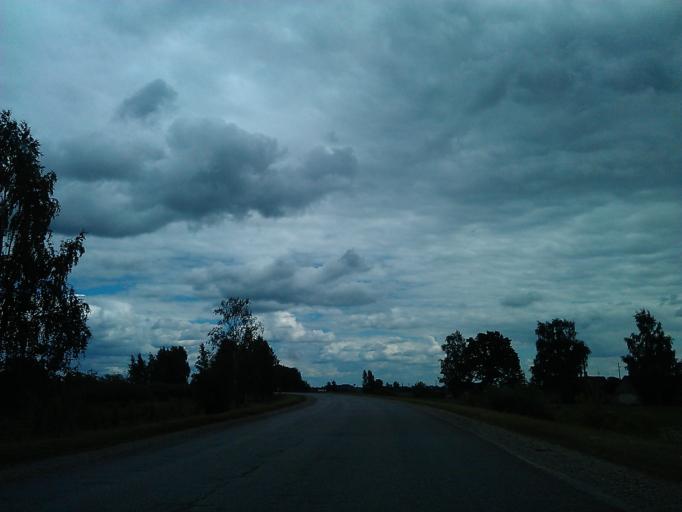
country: LV
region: Dobeles Rajons
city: Dobele
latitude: 56.6196
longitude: 23.3690
